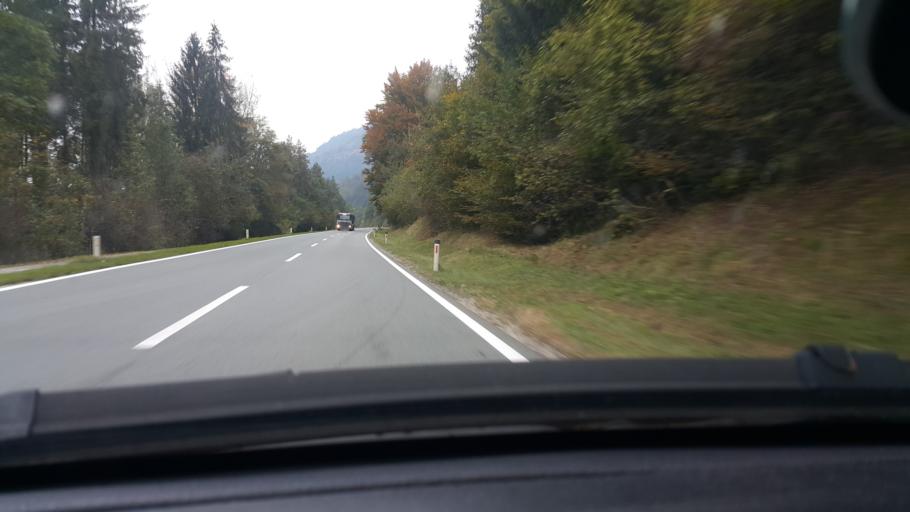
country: AT
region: Carinthia
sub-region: Politischer Bezirk Wolfsberg
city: Lavamund
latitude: 46.6128
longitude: 14.9757
